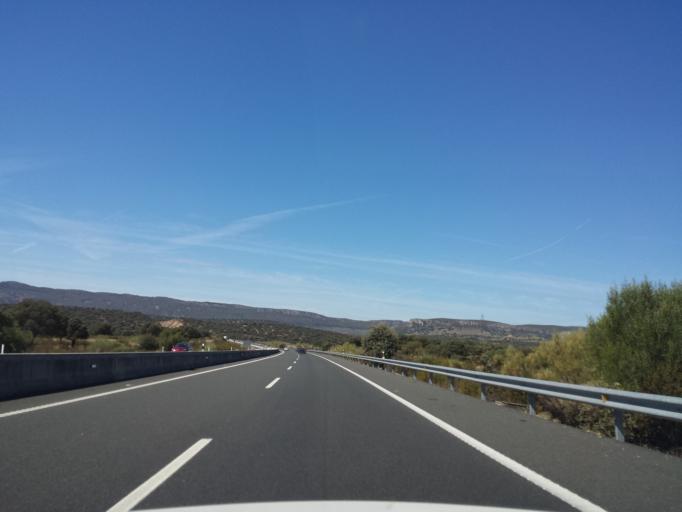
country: ES
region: Extremadura
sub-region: Provincia de Caceres
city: Romangordo
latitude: 39.7861
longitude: -5.7222
